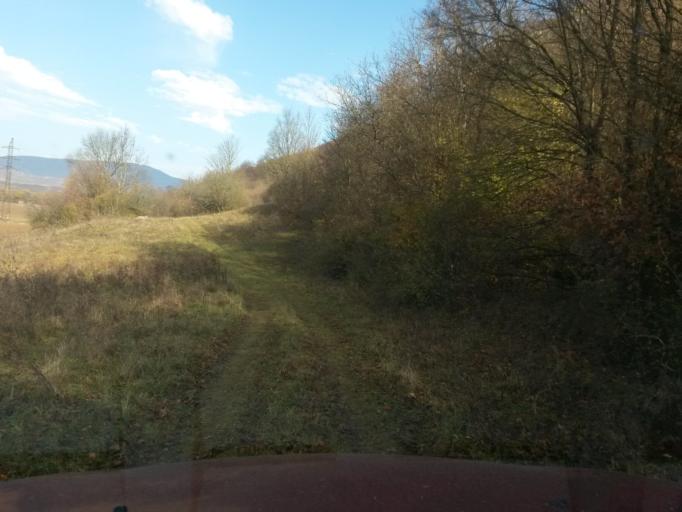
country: SK
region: Kosicky
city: Roznava
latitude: 48.5972
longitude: 20.4845
